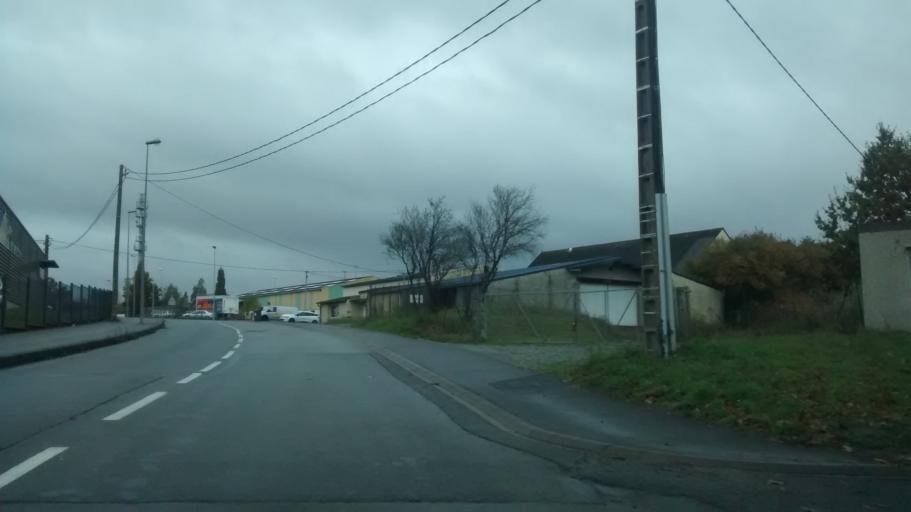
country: FR
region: Brittany
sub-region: Departement d'Ille-et-Vilaine
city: Noyal-sur-Vilaine
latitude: 48.1058
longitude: -1.5188
